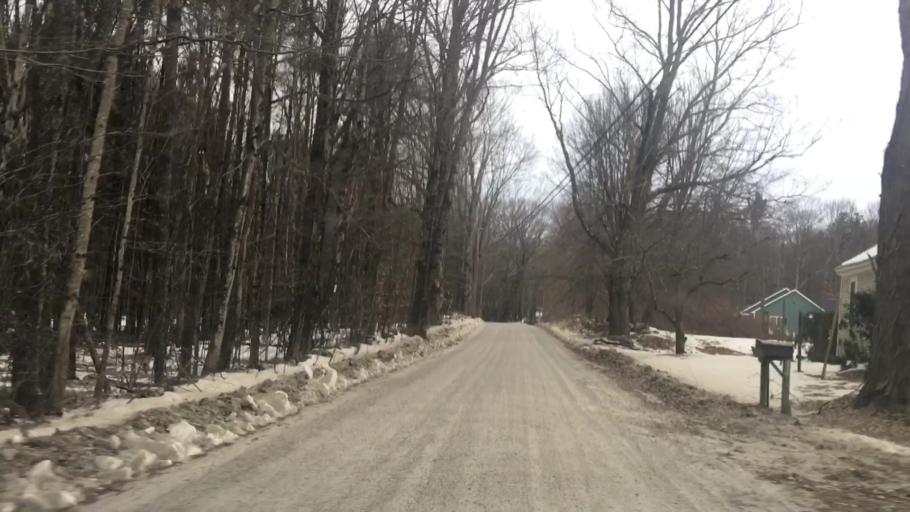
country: US
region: New Hampshire
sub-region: Merrimack County
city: Hopkinton
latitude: 43.1645
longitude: -71.6684
